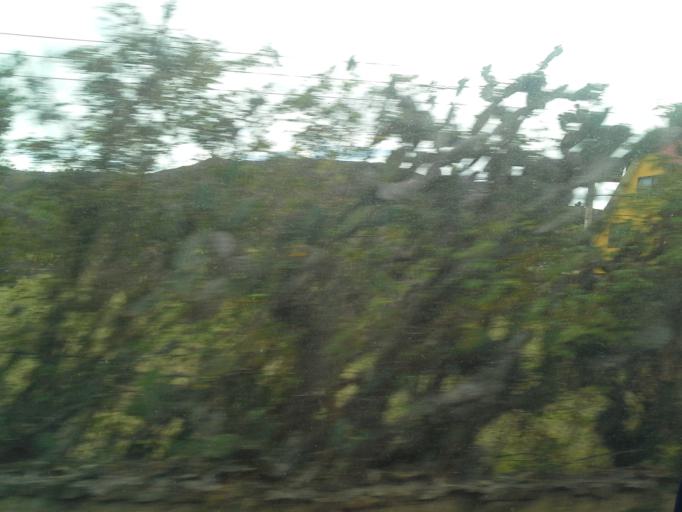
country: CO
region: Boyaca
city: Raquira
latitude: 5.5538
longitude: -73.6402
